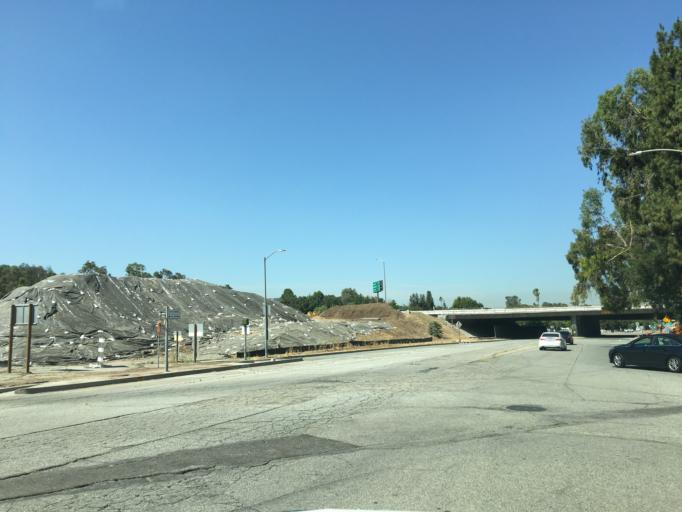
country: US
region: California
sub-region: Los Angeles County
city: Covina
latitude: 34.0710
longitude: -117.8629
